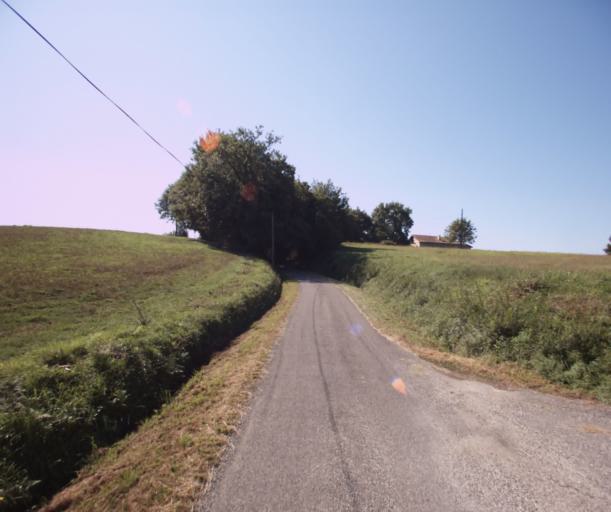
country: FR
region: Midi-Pyrenees
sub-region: Departement du Gers
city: Cazaubon
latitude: 43.9426
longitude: -0.0228
